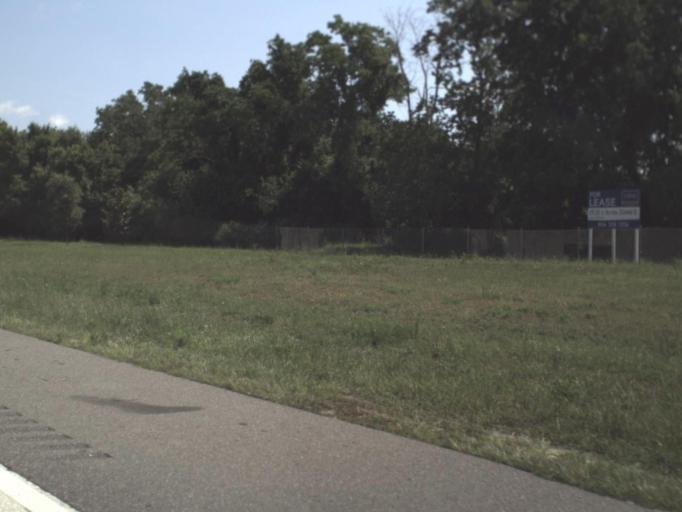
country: US
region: Florida
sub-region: Duval County
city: Jacksonville
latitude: 30.4236
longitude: -81.6564
